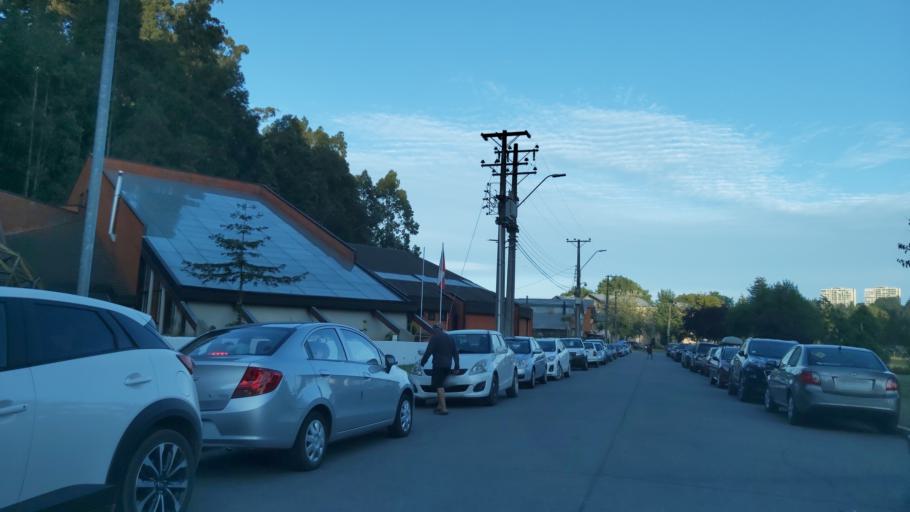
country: CL
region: Biobio
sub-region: Provincia de Concepcion
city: Concepcion
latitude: -36.8454
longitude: -73.1074
